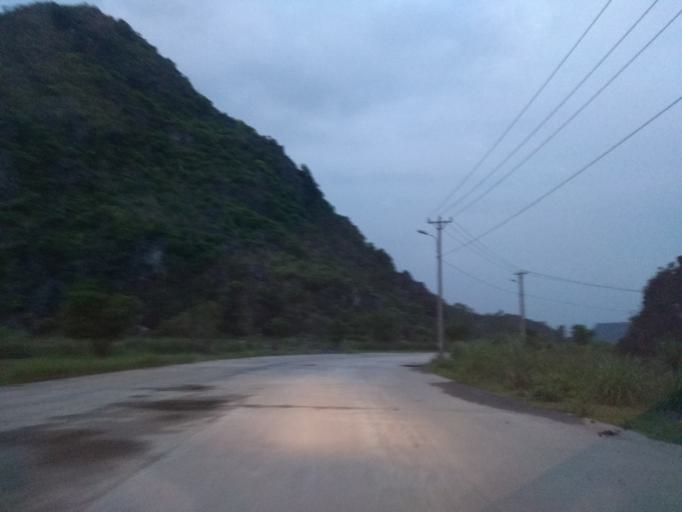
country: VN
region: Ninh Binh
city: Thi Tran Thien Ton
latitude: 20.2807
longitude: 105.9165
